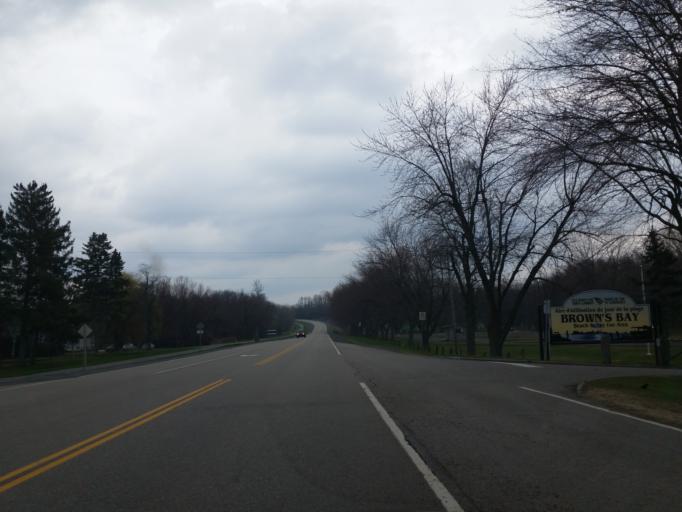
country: CA
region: Ontario
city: Brockville
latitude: 44.4875
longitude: -75.8244
